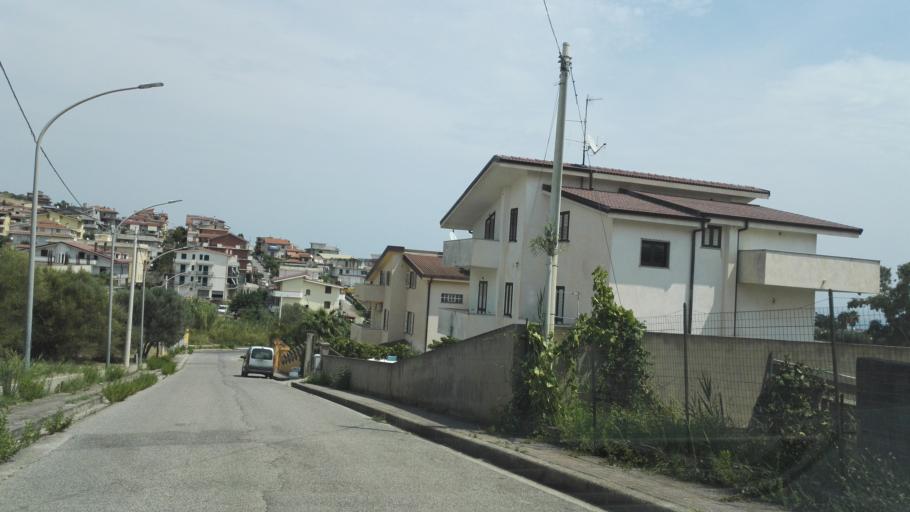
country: IT
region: Calabria
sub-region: Provincia di Reggio Calabria
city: Riace Marina
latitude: 38.3867
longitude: 16.5226
